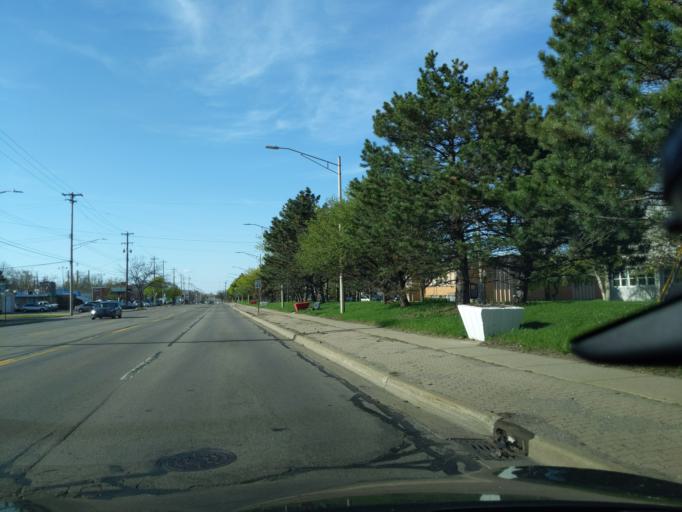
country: US
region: Michigan
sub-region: Ingham County
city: Lansing
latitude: 42.6869
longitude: -84.5480
